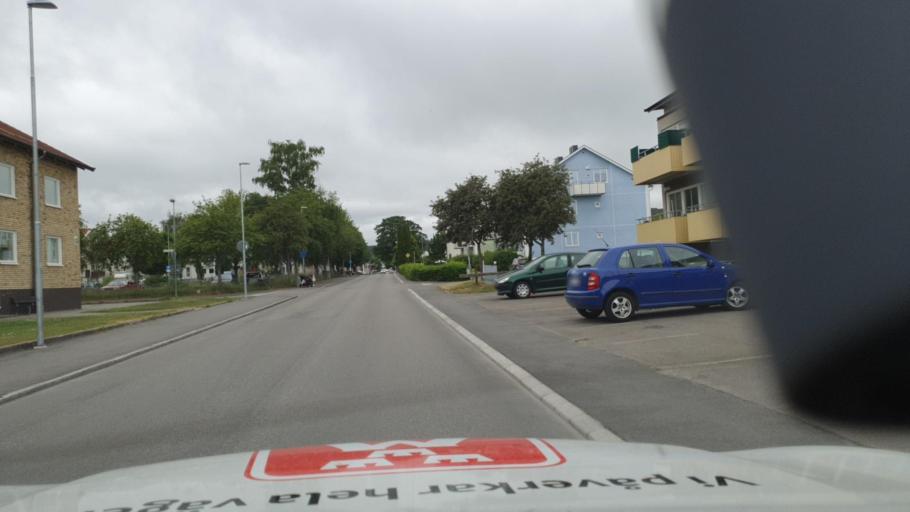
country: SE
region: Joenkoeping
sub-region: Habo Kommun
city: Habo
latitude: 57.9098
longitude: 14.0805
